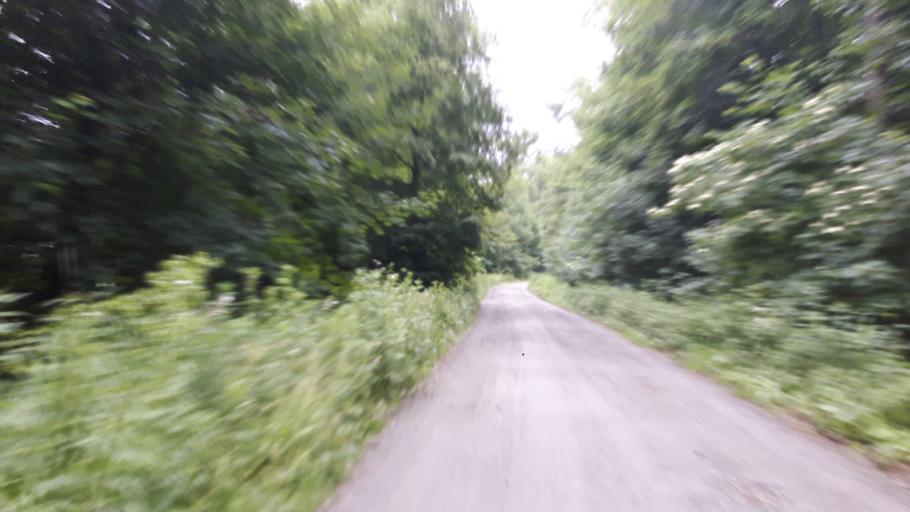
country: PL
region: Warmian-Masurian Voivodeship
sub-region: Powiat elblaski
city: Tolkmicko
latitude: 54.3351
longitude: 19.5524
